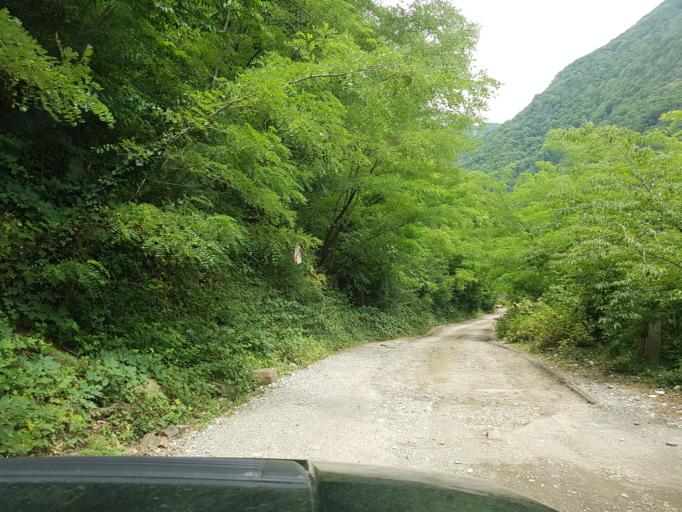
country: GE
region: Imereti
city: Kutaisi
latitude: 42.4238
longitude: 42.7375
